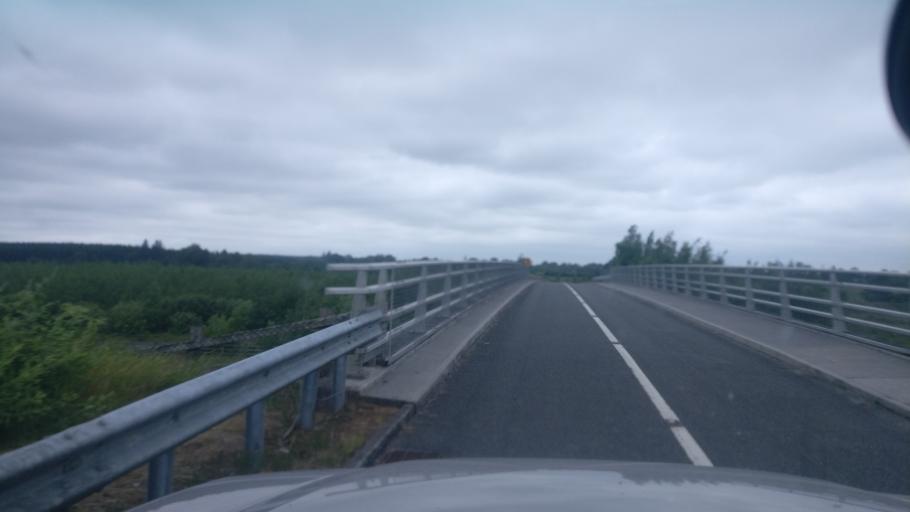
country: IE
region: Connaught
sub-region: County Galway
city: Ballinasloe
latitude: 53.2907
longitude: -8.3758
